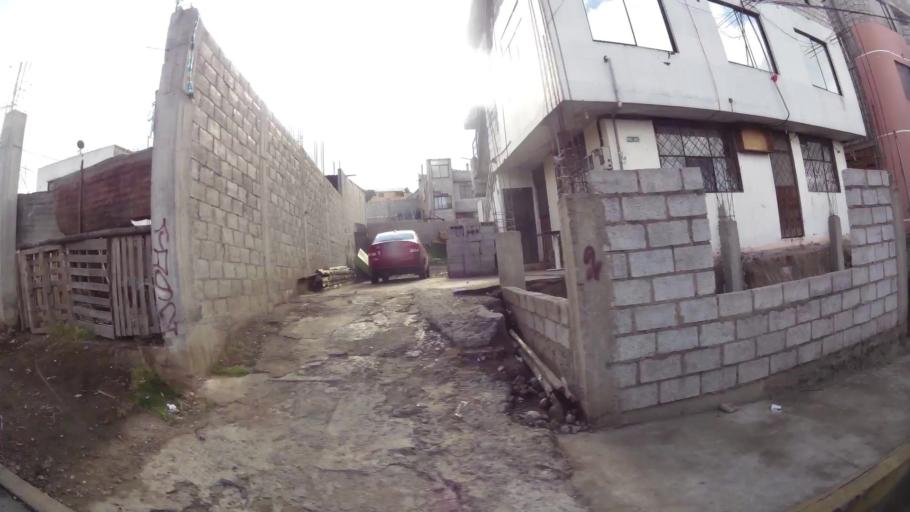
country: EC
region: Pichincha
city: Quito
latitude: -0.1366
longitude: -78.4577
